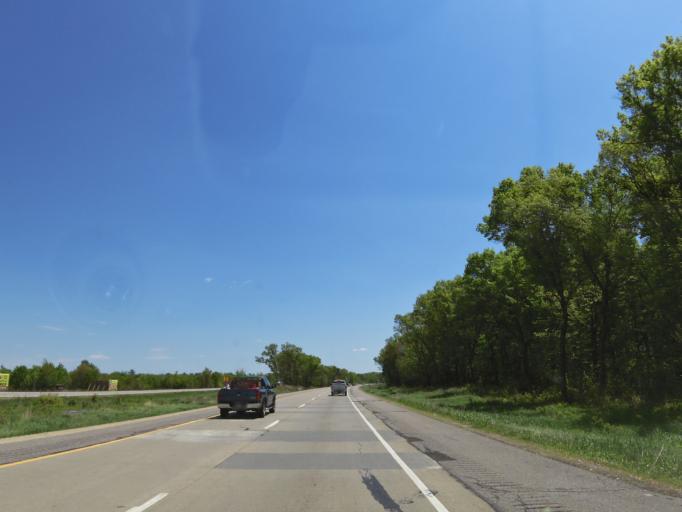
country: US
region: Wisconsin
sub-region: Juneau County
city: New Lisbon
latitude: 43.8741
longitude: -90.1300
